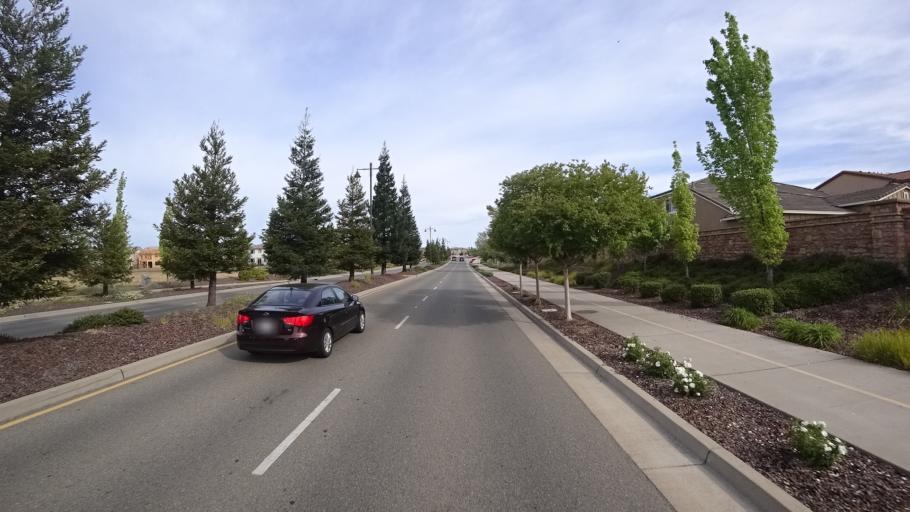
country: US
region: California
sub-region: Placer County
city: Rocklin
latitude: 38.8274
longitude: -121.2863
